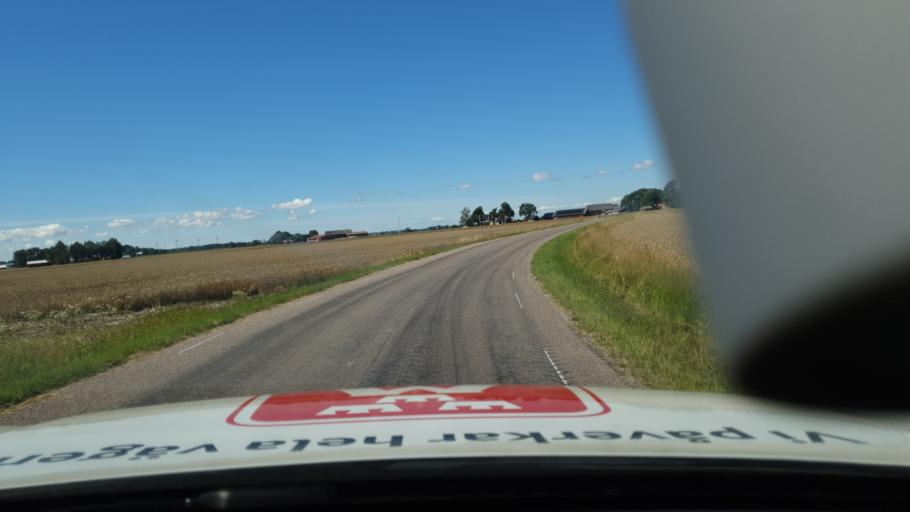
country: SE
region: Vaestra Goetaland
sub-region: Lidkopings Kommun
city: Vinninga
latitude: 58.3816
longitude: 13.2759
